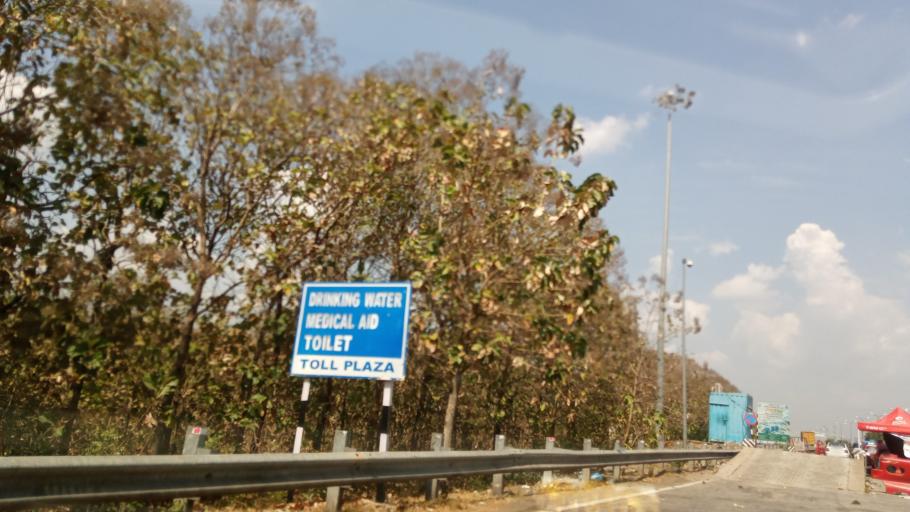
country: IN
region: Tamil Nadu
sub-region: Vellore
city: Pallikondai
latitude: 12.9061
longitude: 78.9521
